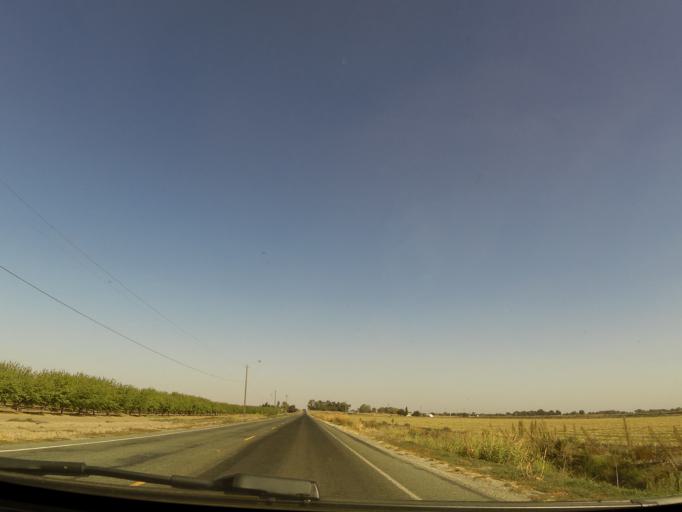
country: US
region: California
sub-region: San Joaquin County
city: Country Club
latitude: 37.8771
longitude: -121.3949
